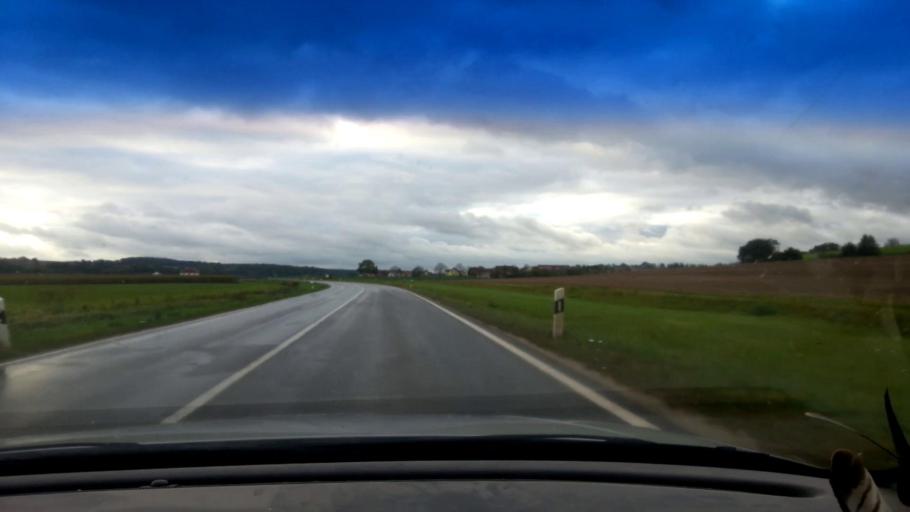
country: DE
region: Bavaria
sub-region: Upper Franconia
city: Burgebrach
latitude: 49.8215
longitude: 10.6739
